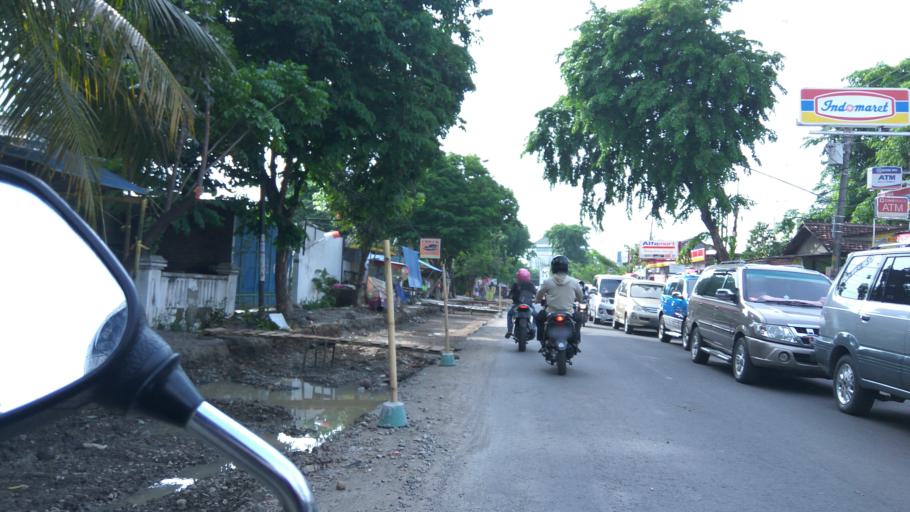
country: ID
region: Central Java
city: Mranggen
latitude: -7.0237
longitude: 110.4647
